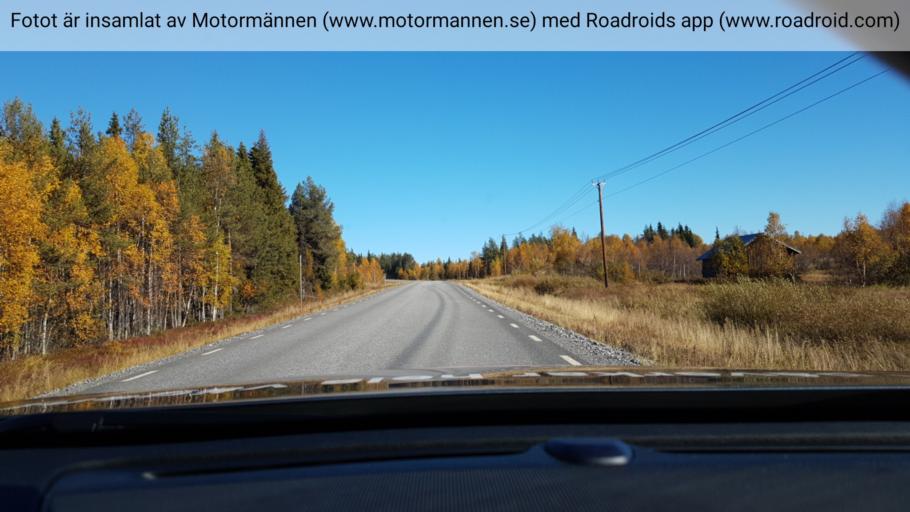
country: SE
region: Norrbotten
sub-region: Gallivare Kommun
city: Gaellivare
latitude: 66.7672
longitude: 21.0405
